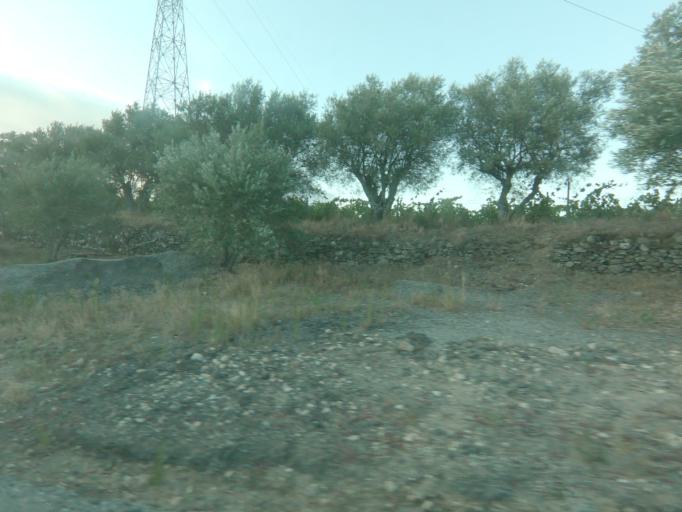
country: PT
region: Vila Real
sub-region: Peso da Regua
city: Peso da Regua
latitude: 41.1391
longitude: -7.7441
